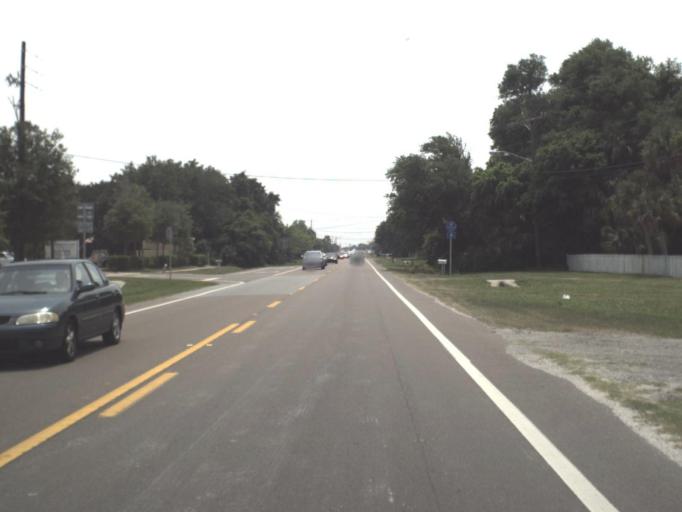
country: US
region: Florida
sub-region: Duval County
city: Atlantic Beach
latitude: 30.4028
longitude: -81.4320
